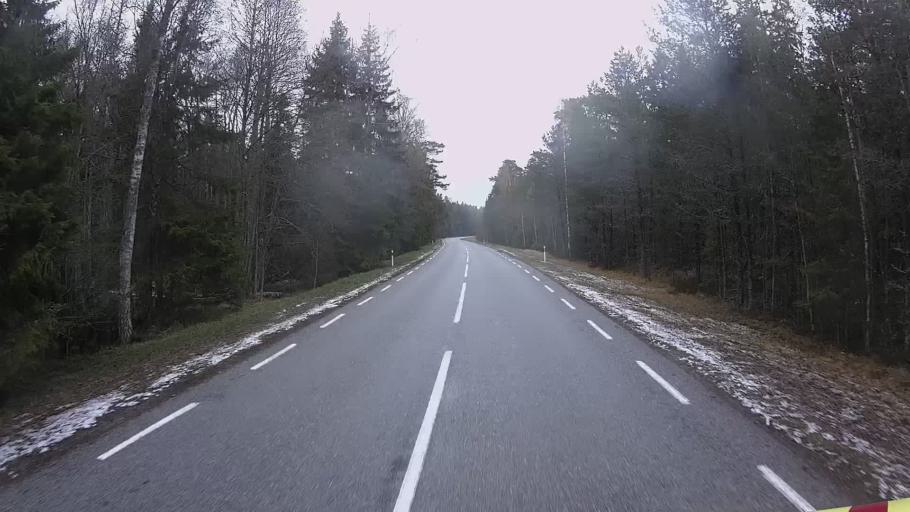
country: EE
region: Hiiumaa
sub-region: Kaerdla linn
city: Kardla
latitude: 59.0506
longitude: 22.6819
